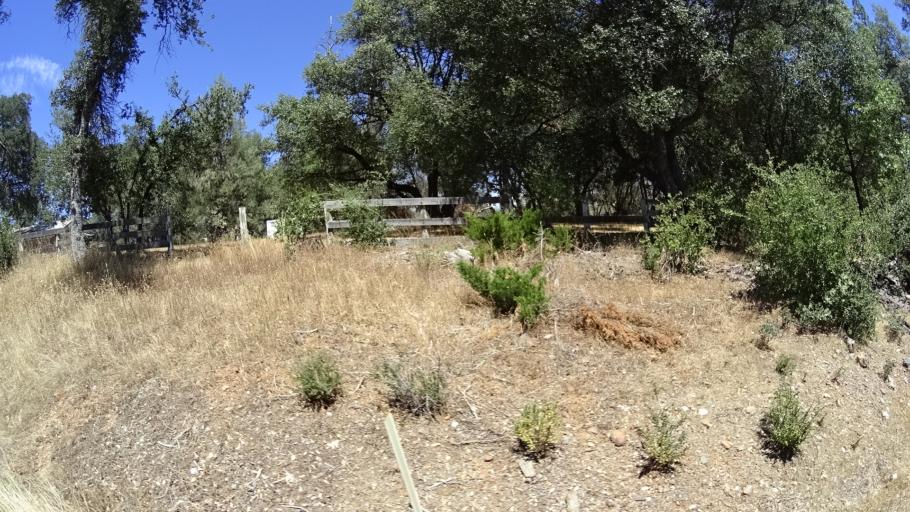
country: US
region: California
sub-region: Calaveras County
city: Mountain Ranch
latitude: 38.2433
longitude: -120.5115
